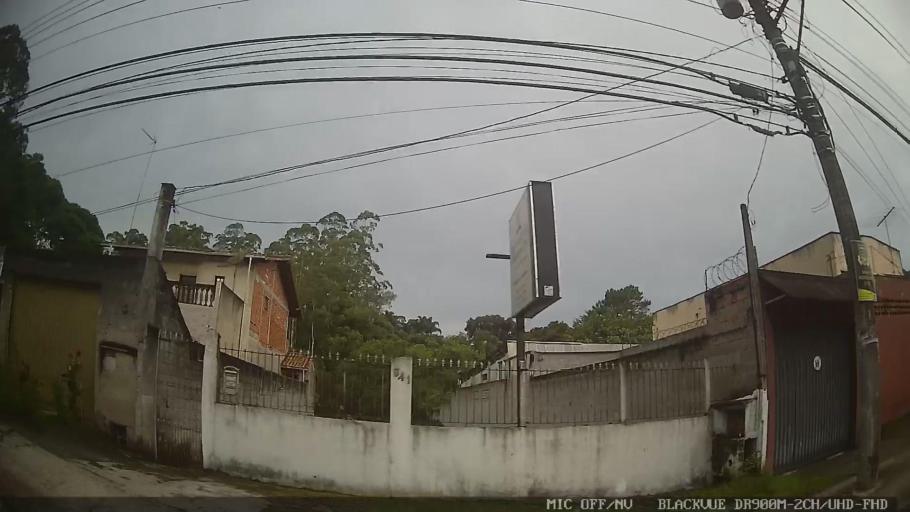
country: BR
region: Sao Paulo
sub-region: Ribeirao Pires
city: Ribeirao Pires
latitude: -23.6823
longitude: -46.3531
